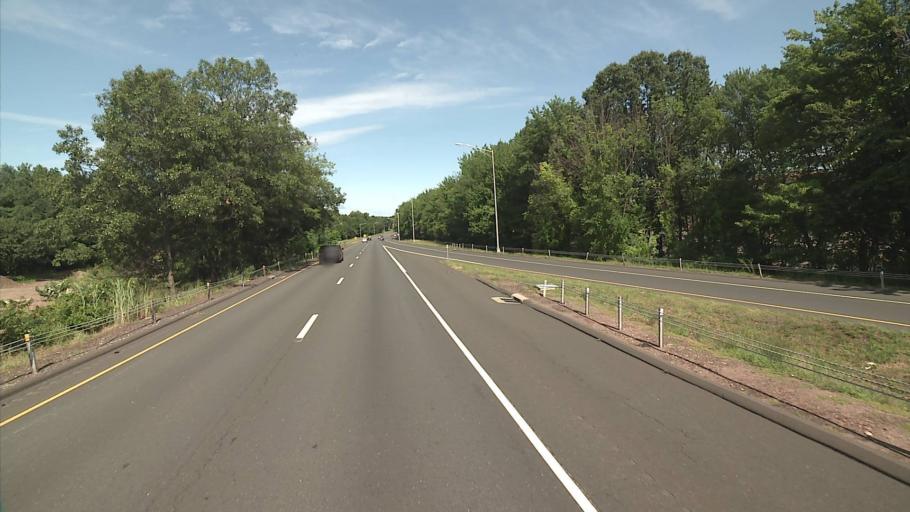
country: US
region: Connecticut
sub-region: Hartford County
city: Glastonbury
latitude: 41.7150
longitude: -72.5958
